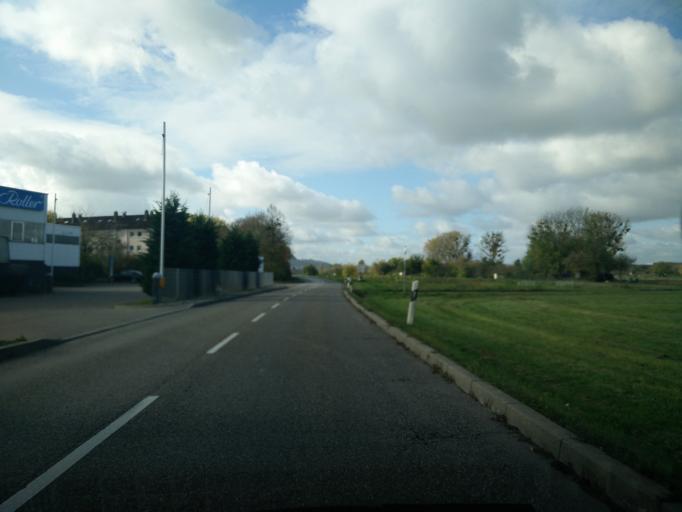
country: DE
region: Baden-Wuerttemberg
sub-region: Regierungsbezirk Stuttgart
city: Gerlingen
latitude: 48.8097
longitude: 9.0865
